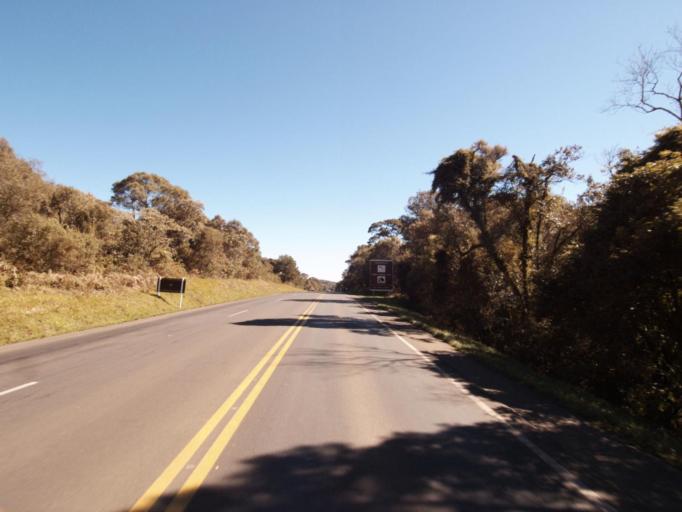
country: BR
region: Santa Catarina
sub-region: Concordia
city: Concordia
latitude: -26.9725
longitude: -51.8452
